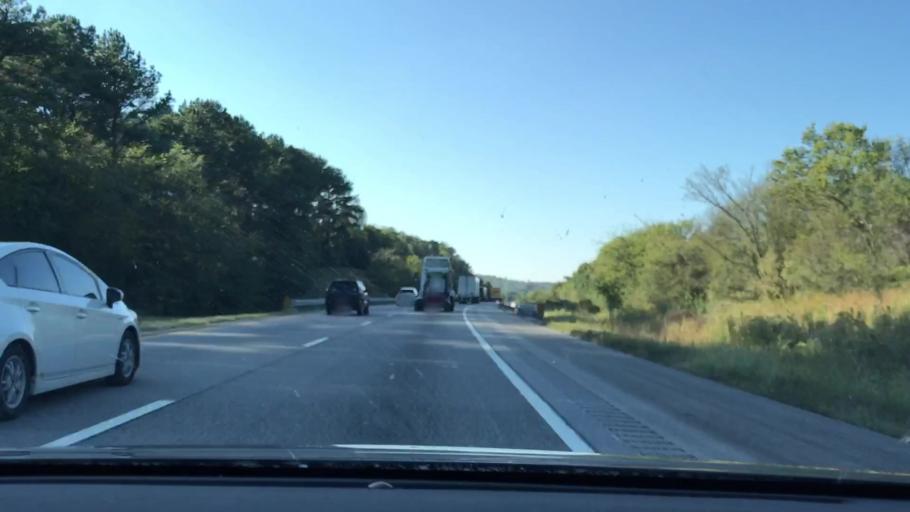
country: US
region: Tennessee
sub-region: Smith County
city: Gordonsville
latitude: 36.1665
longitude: -85.9002
